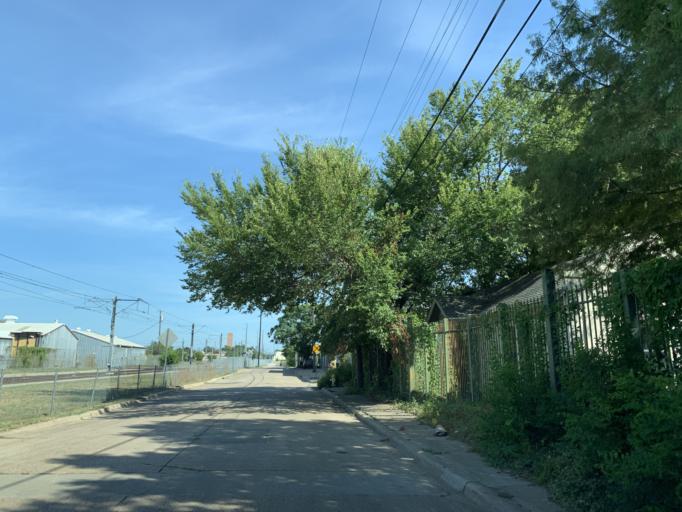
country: US
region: Texas
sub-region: Dallas County
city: Dallas
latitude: 32.7779
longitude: -96.7697
